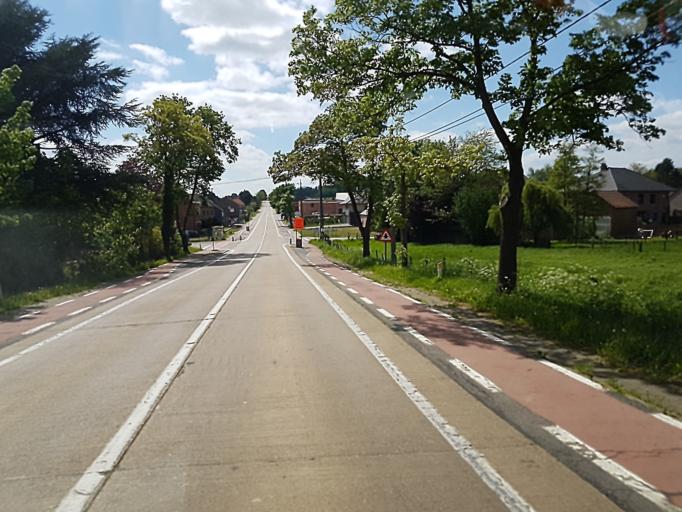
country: BE
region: Flanders
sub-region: Provincie Vlaams-Brabant
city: Glabbeek-Zuurbemde
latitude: 50.8922
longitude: 4.9697
